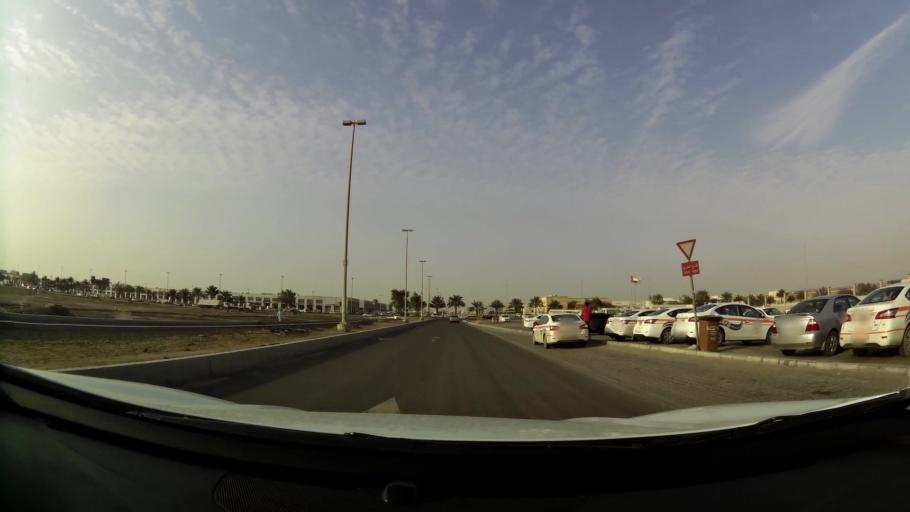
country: AE
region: Abu Dhabi
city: Abu Dhabi
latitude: 24.3449
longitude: 54.5174
